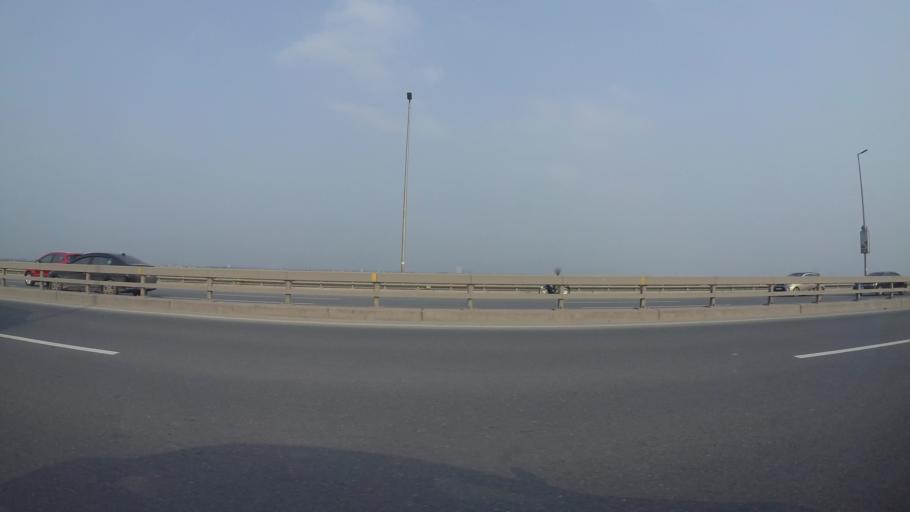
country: VN
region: Ha Noi
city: Tay Ho
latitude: 21.1023
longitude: 105.8250
